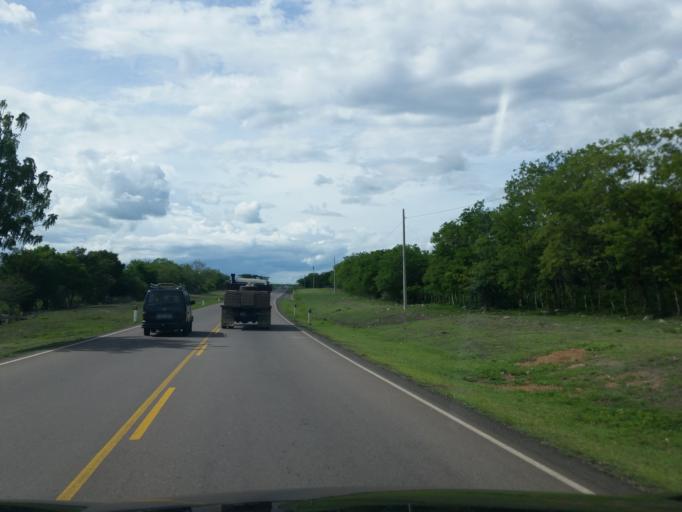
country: NI
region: Matagalpa
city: Ciudad Dario
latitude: 12.7092
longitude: -86.0922
